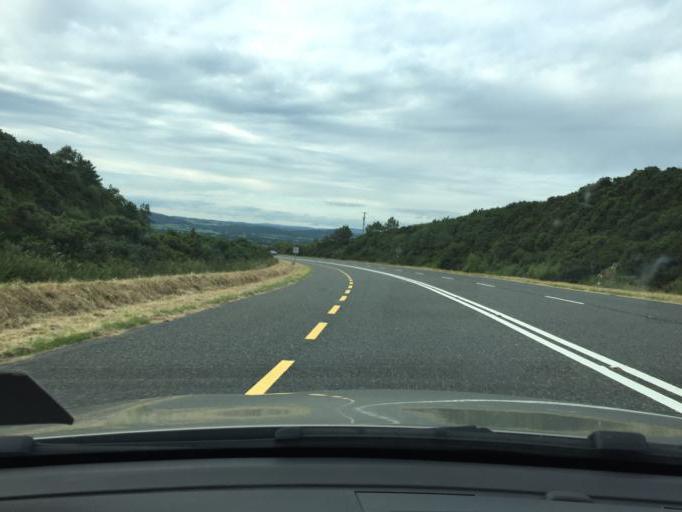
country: IE
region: Munster
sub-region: Waterford
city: Dungarvan
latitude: 52.0572
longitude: -7.6651
